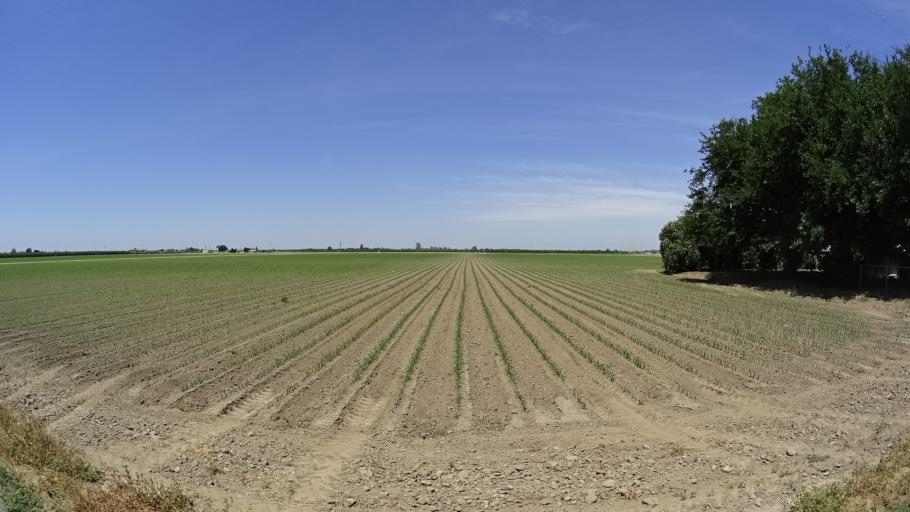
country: US
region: California
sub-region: Kings County
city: Armona
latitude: 36.2839
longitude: -119.7048
